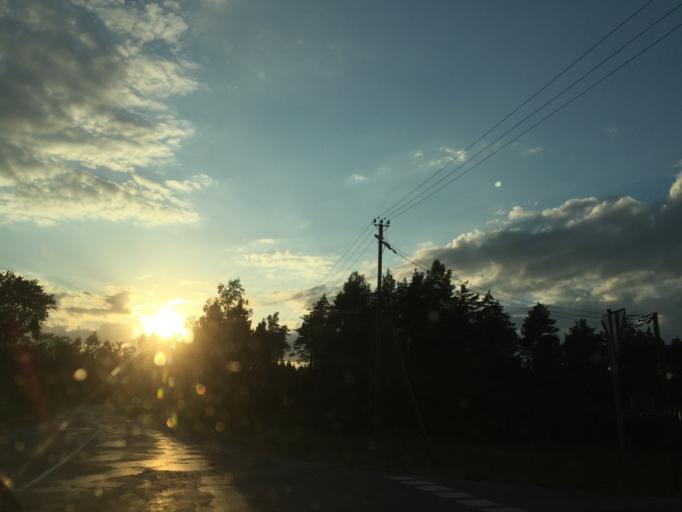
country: LV
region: Sigulda
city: Sigulda
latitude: 57.1106
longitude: 24.9222
